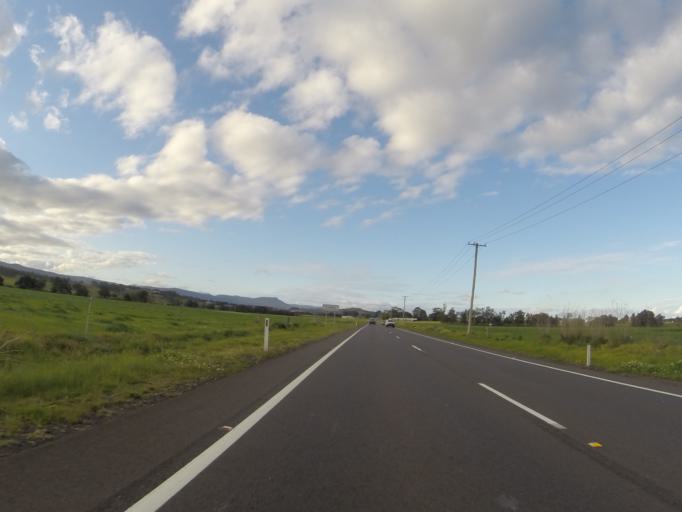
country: AU
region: New South Wales
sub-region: Shellharbour
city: Albion Park Rail
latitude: -34.5588
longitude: 150.7788
